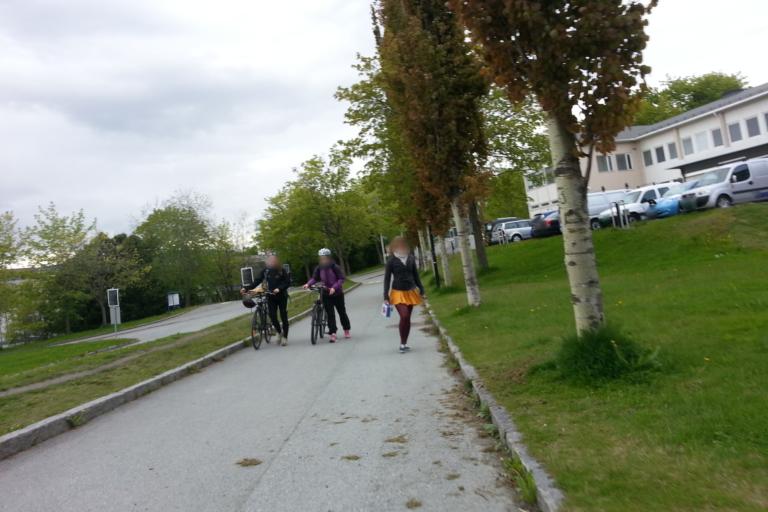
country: NO
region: Sor-Trondelag
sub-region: Trondheim
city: Trondheim
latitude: 63.4146
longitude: 10.4109
